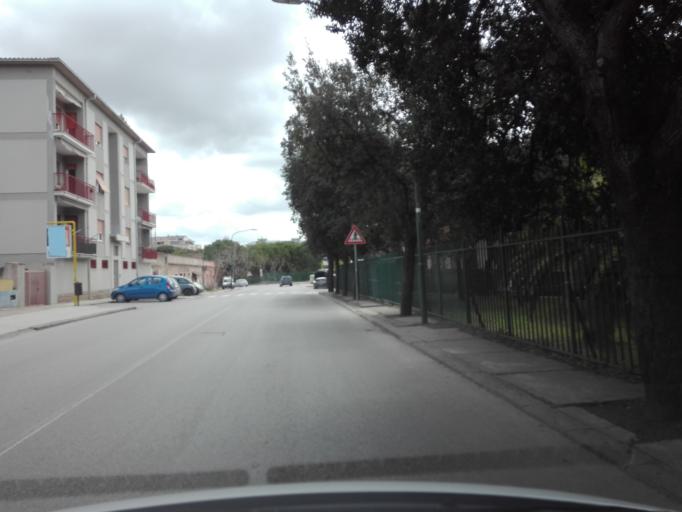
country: IT
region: Sardinia
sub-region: Provincia di Sassari
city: Sassari
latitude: 40.7398
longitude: 8.5586
